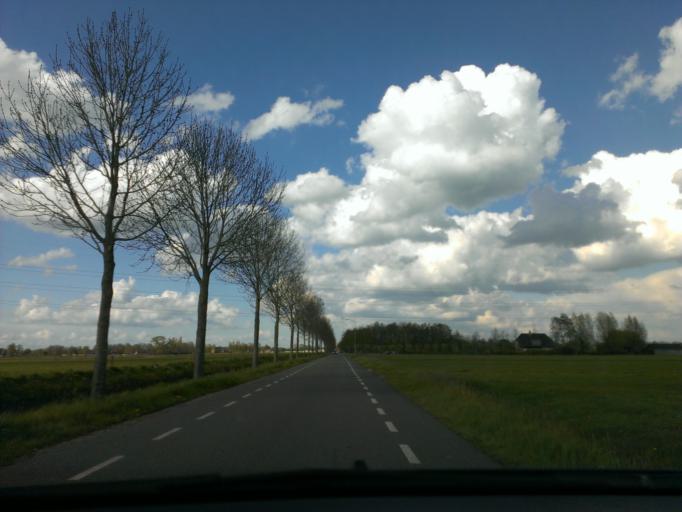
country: NL
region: Gelderland
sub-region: Gemeente Epe
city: Oene
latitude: 52.3120
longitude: 6.0221
